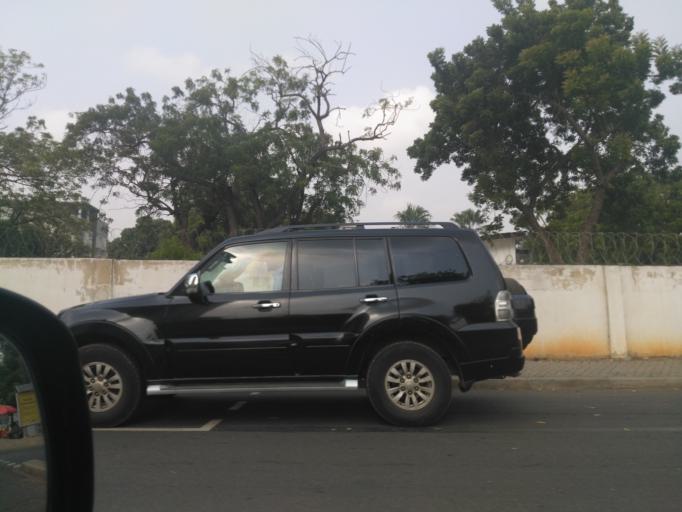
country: GH
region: Greater Accra
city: Accra
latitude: 5.6012
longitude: -0.1877
